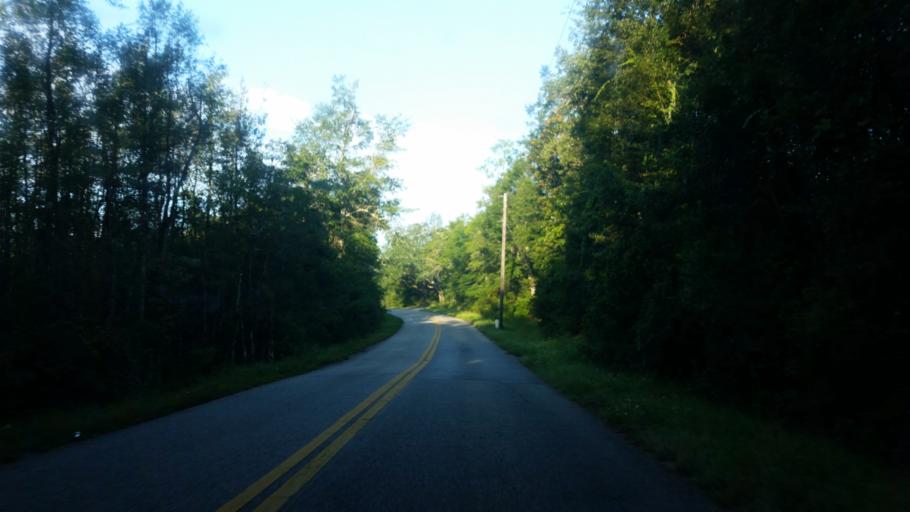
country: US
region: Florida
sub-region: Santa Rosa County
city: East Milton
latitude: 30.6304
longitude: -87.0217
